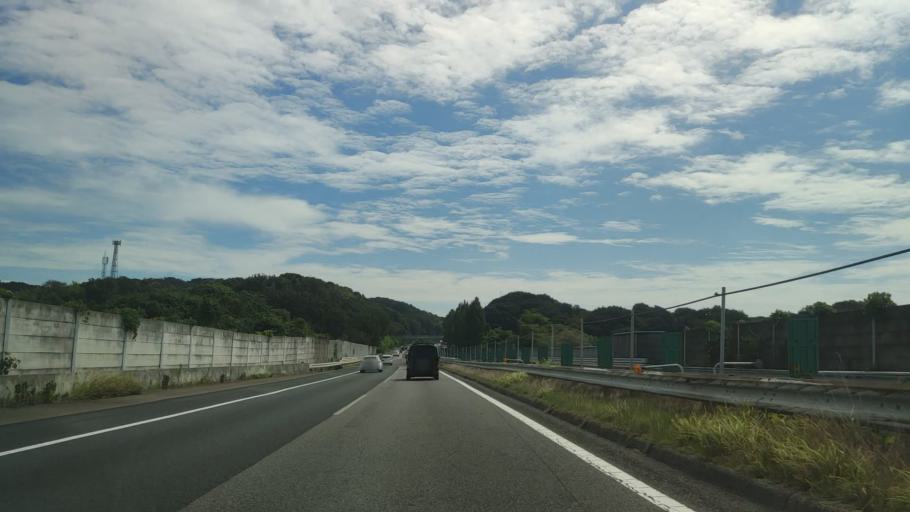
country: JP
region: Aichi
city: Okazaki
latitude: 35.0002
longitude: 137.1782
